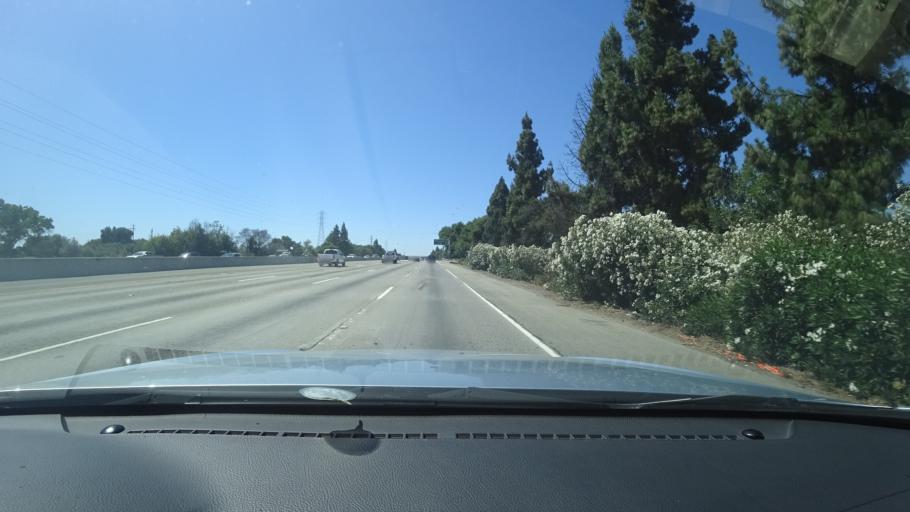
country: US
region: California
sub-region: Santa Clara County
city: Alum Rock
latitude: 37.3792
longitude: -121.8571
